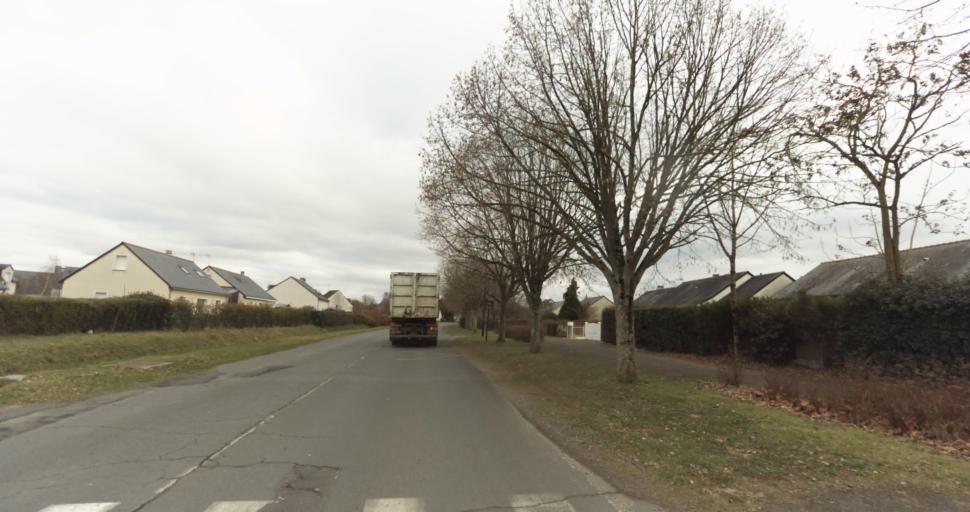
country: FR
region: Pays de la Loire
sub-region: Departement de Maine-et-Loire
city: Saumur
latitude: 47.2759
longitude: -0.0738
